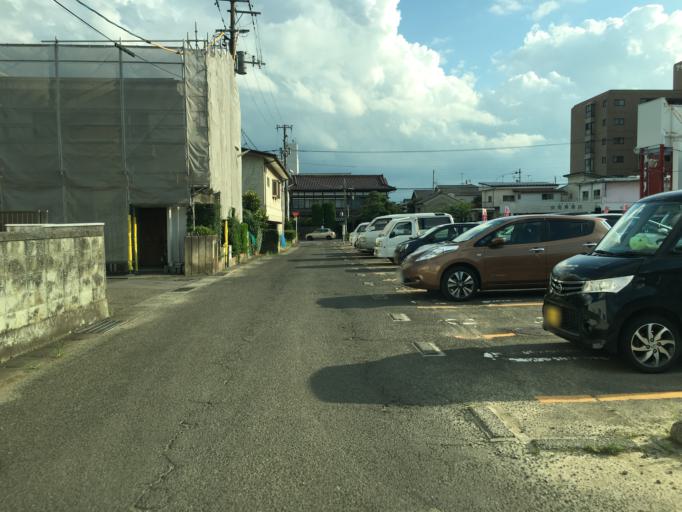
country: JP
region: Fukushima
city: Fukushima-shi
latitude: 37.7632
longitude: 140.4444
